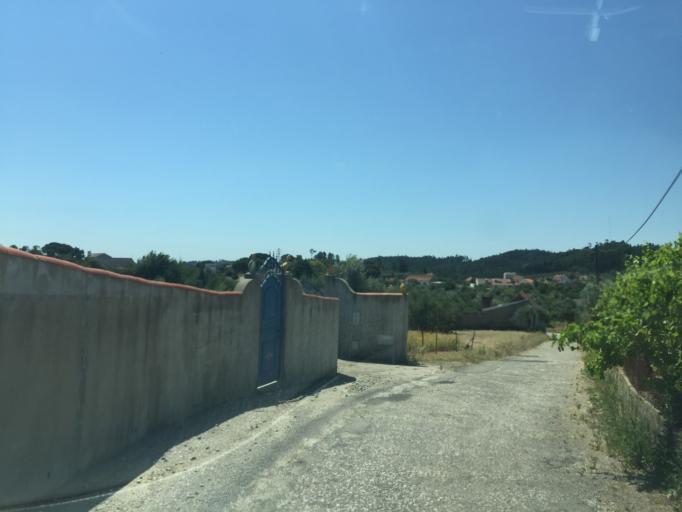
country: PT
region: Santarem
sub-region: Ferreira do Zezere
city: Ferreira do Zezere
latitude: 39.6213
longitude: -8.3132
